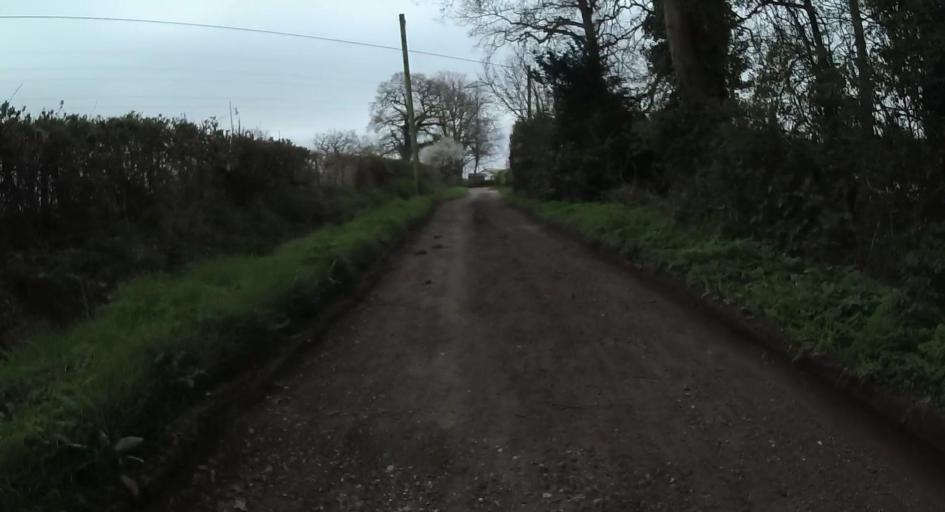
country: GB
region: England
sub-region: West Berkshire
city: Arborfield
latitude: 51.4044
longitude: -0.9103
